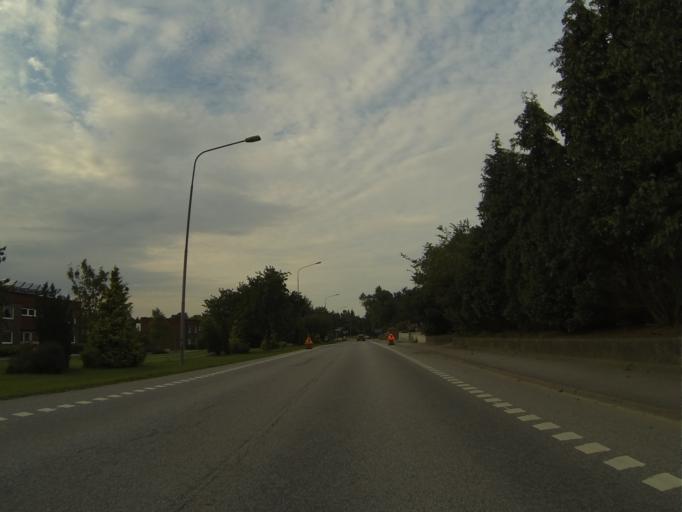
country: SE
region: Skane
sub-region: Lunds Kommun
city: Genarp
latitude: 55.6740
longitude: 13.3511
